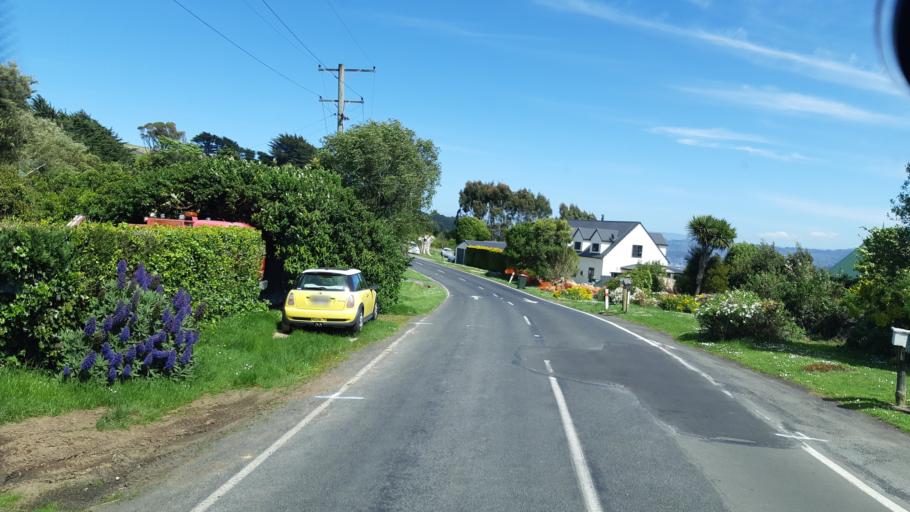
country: NZ
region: Otago
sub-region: Dunedin City
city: Portobello
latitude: -45.8757
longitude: 170.6229
